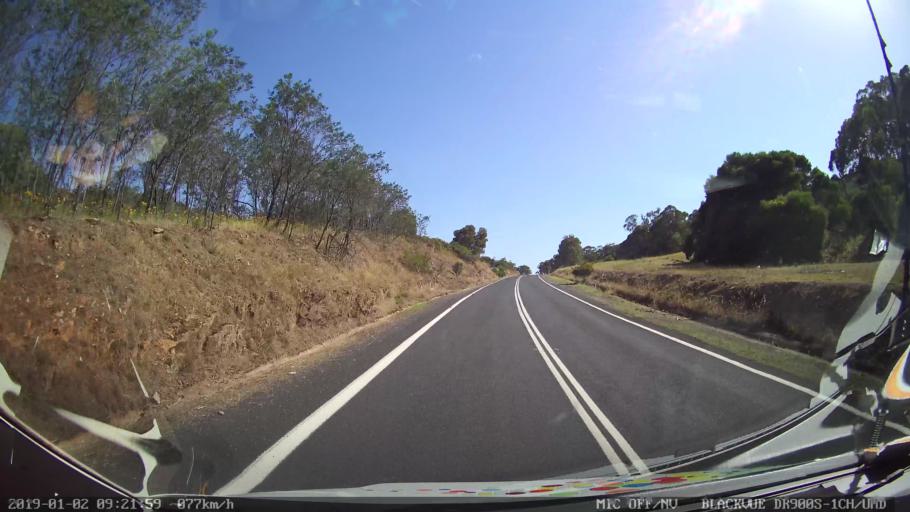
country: AU
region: New South Wales
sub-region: Tumut Shire
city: Tumut
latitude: -35.3995
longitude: 148.2891
